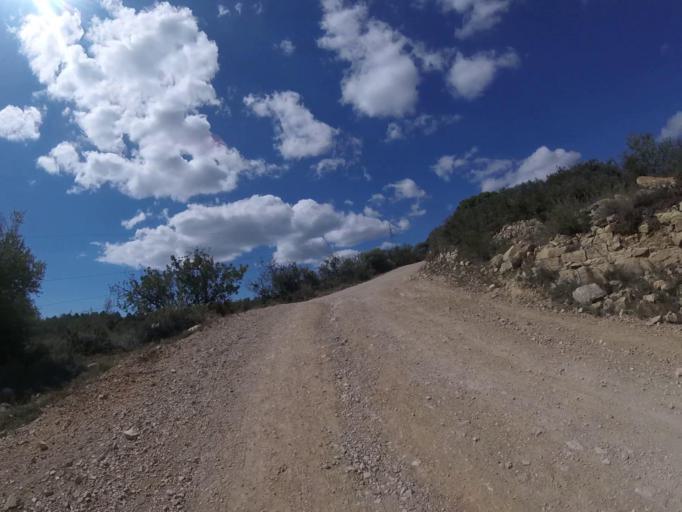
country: ES
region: Valencia
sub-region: Provincia de Castello
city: Santa Magdalena de Pulpis
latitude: 40.3268
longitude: 0.3542
